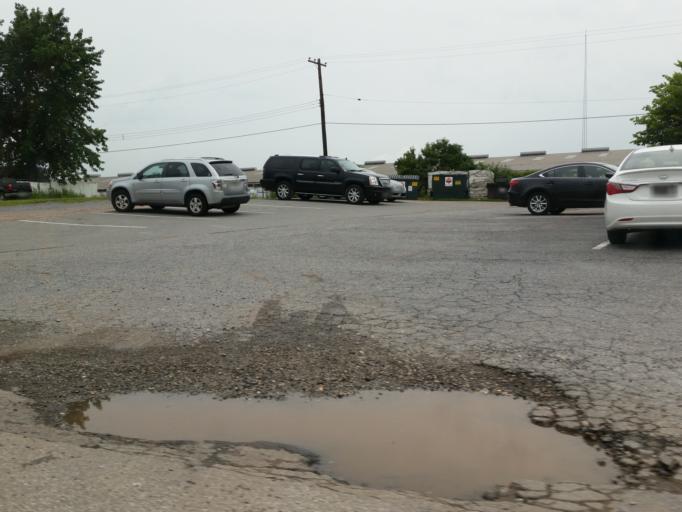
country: US
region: Pennsylvania
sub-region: York County
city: Emigsville
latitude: 40.0205
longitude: -76.7475
